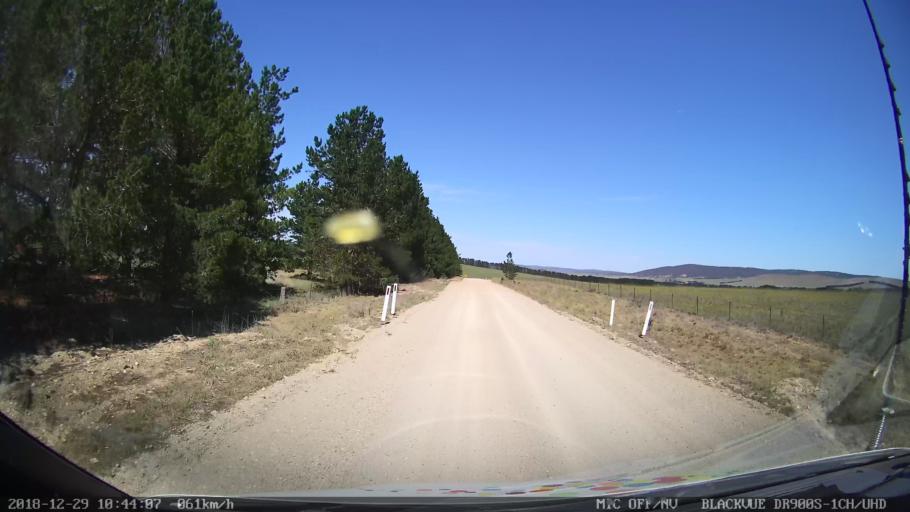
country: AU
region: New South Wales
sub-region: Palerang
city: Bungendore
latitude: -35.0413
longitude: 149.5314
